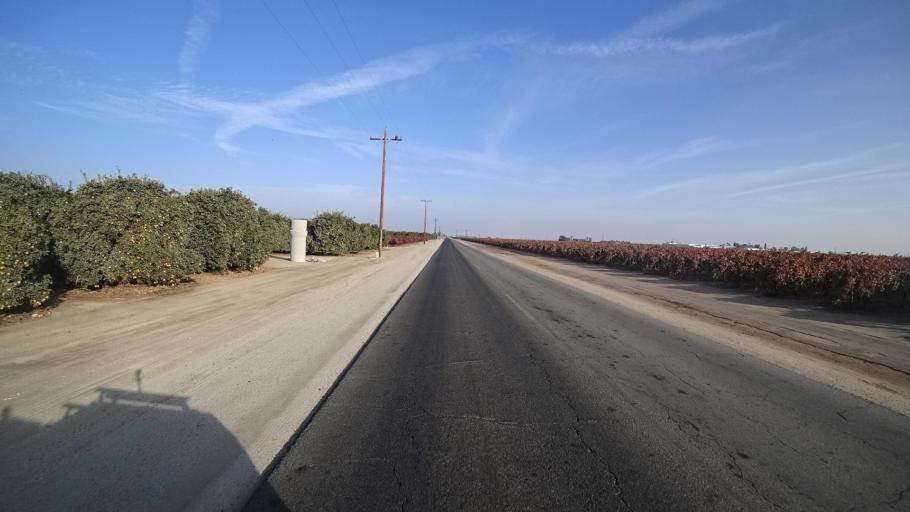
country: US
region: California
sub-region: Kern County
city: Delano
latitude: 35.7653
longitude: -119.1875
